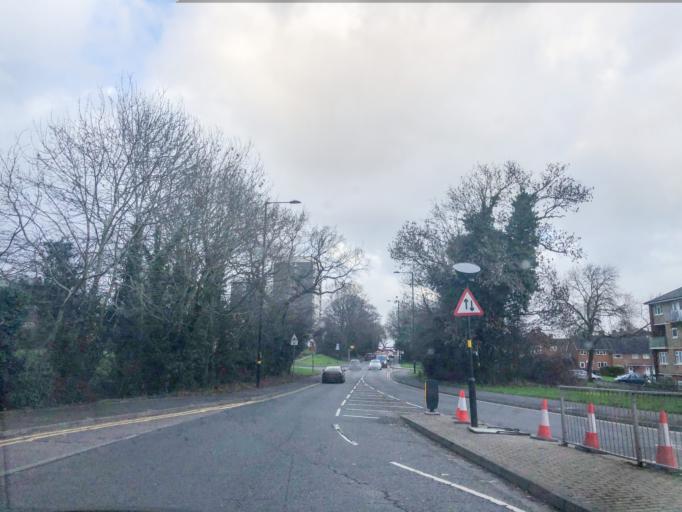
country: GB
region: England
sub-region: Solihull
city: Tidbury Green
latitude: 52.4074
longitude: -1.8882
